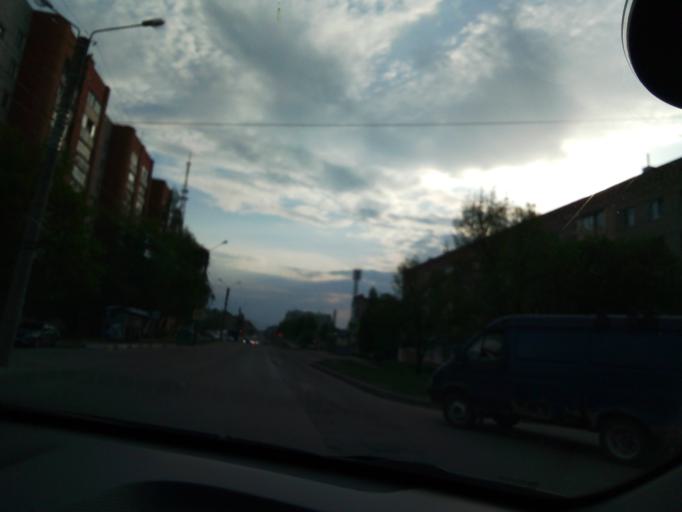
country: RU
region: Chuvashia
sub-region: Cheboksarskiy Rayon
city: Cheboksary
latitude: 56.1225
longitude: 47.2740
